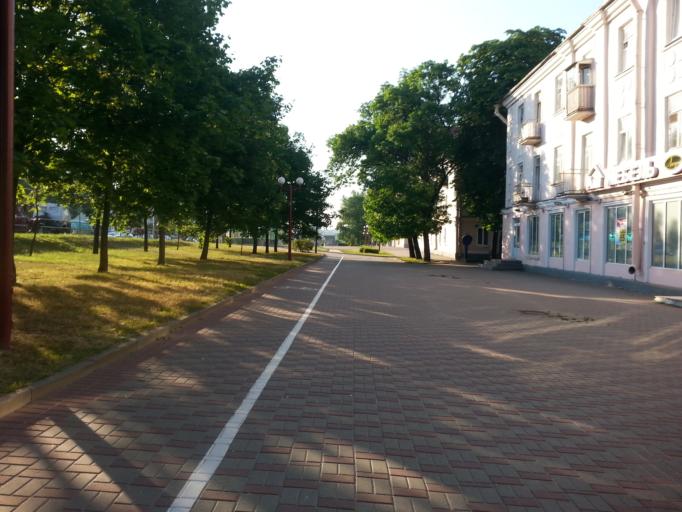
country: BY
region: Minsk
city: Vyaliki Trastsyanets
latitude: 53.8670
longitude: 27.6547
